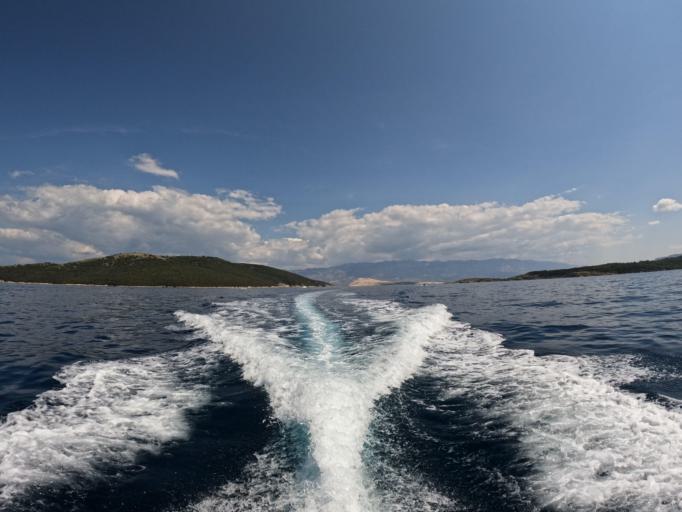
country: HR
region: Primorsko-Goranska
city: Lopar
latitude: 44.8564
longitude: 14.7339
